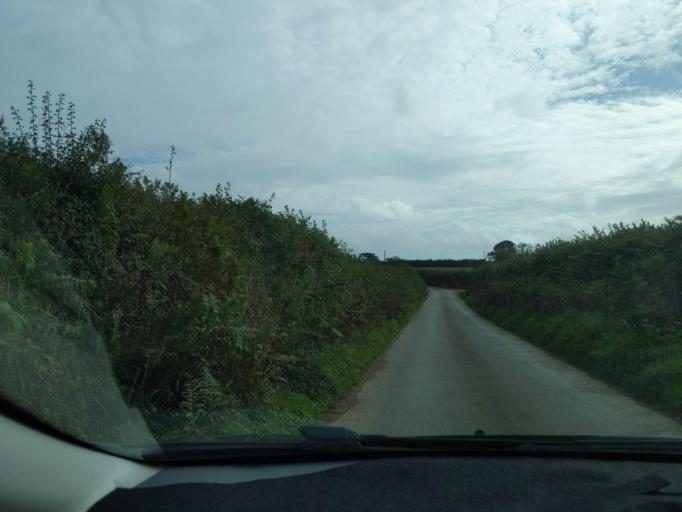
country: GB
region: England
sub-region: Cornwall
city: Mevagissey
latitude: 50.2790
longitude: -4.8308
